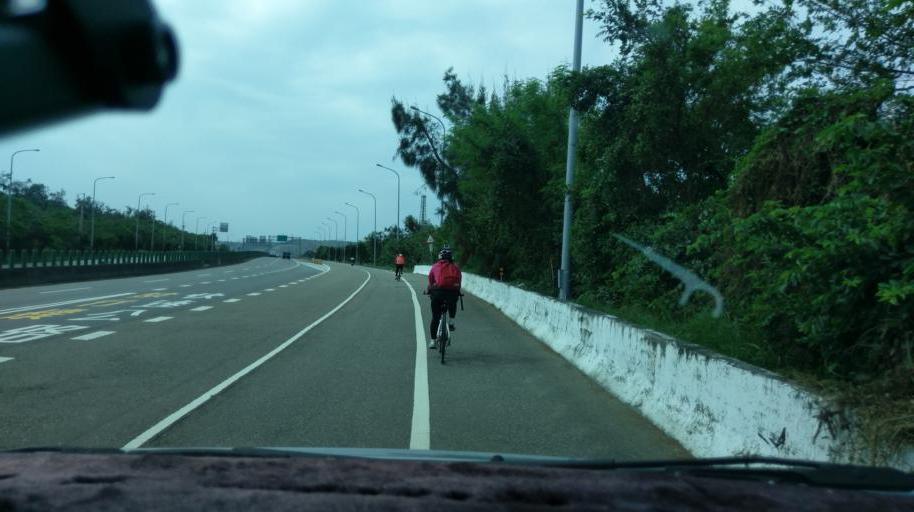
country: TW
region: Taiwan
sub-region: Miaoli
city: Miaoli
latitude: 24.6107
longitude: 120.7532
